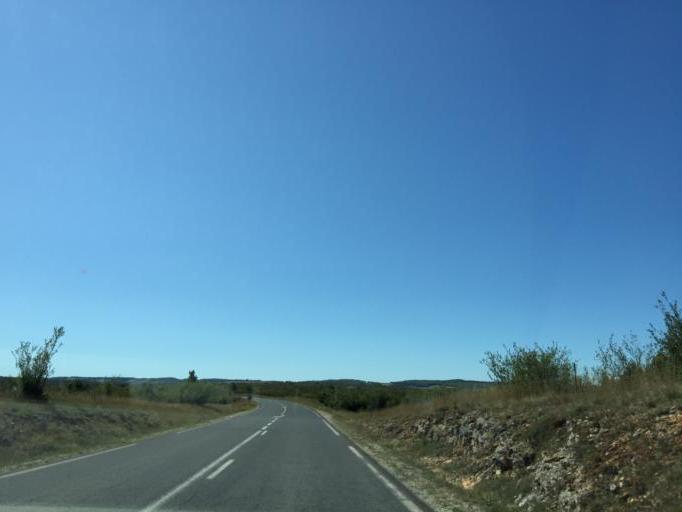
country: FR
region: Midi-Pyrenees
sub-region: Departement de l'Aveyron
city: La Cavalerie
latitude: 43.9488
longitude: 3.2141
